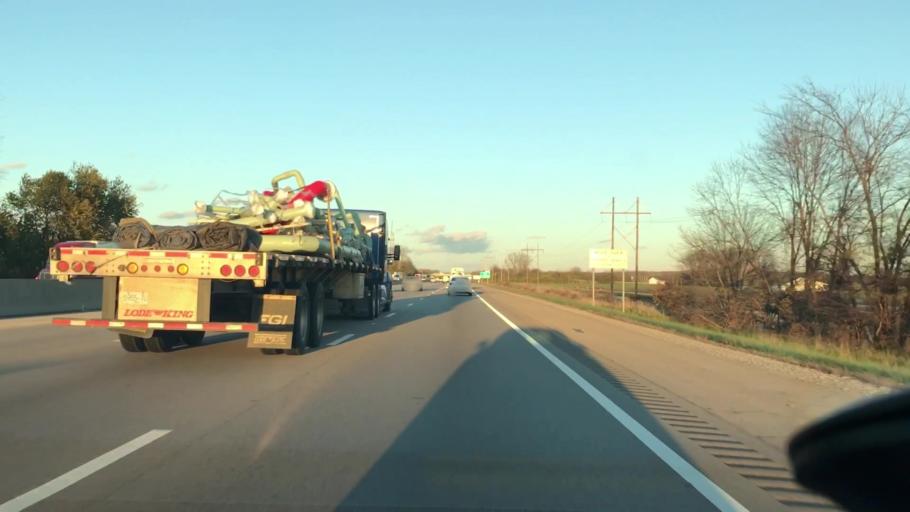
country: US
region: Ohio
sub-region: Clark County
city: Holiday Valley
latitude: 39.8730
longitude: -83.9764
